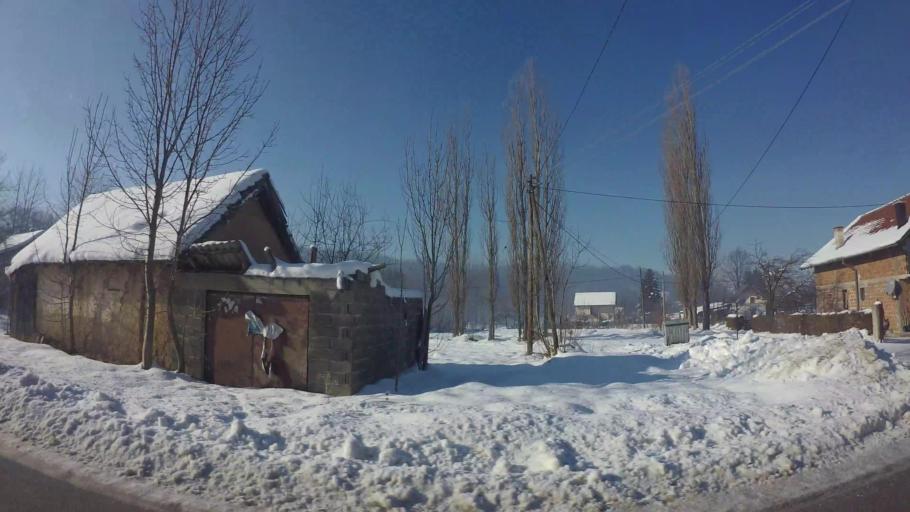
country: BA
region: Federation of Bosnia and Herzegovina
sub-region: Kanton Sarajevo
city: Sarajevo
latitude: 43.8172
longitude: 18.3830
